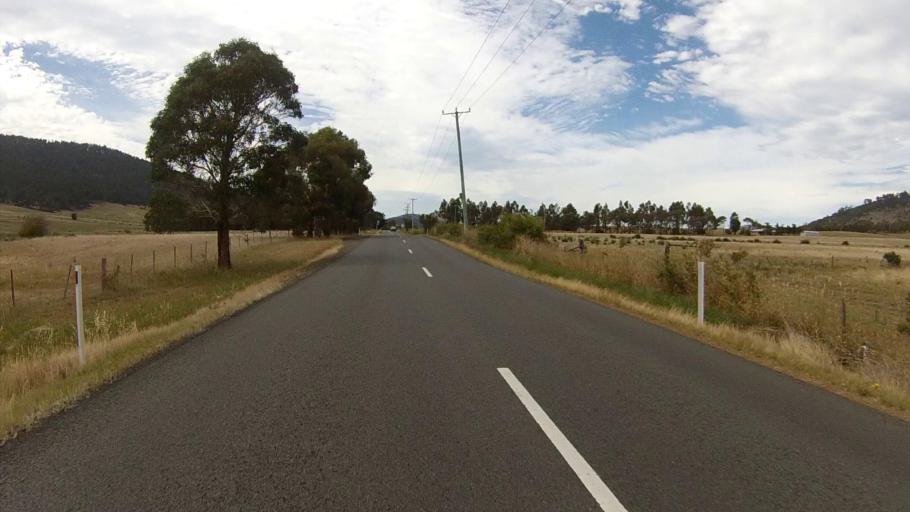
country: AU
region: Tasmania
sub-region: Brighton
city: Old Beach
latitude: -42.7139
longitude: 147.3812
